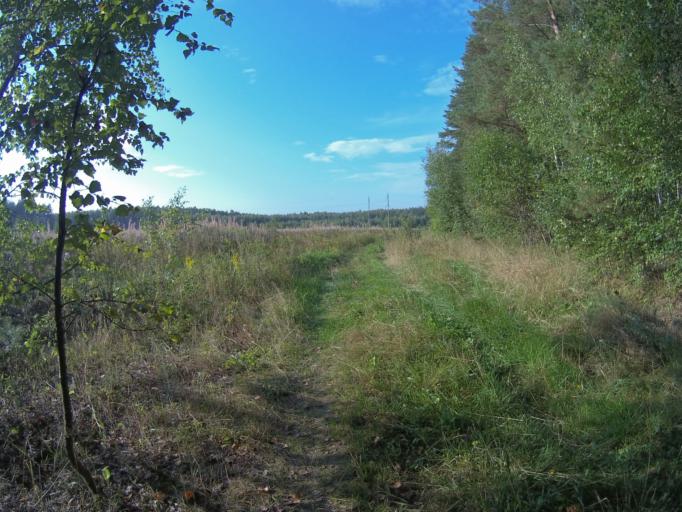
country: RU
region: Vladimir
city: Raduzhnyy
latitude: 56.0121
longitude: 40.2935
